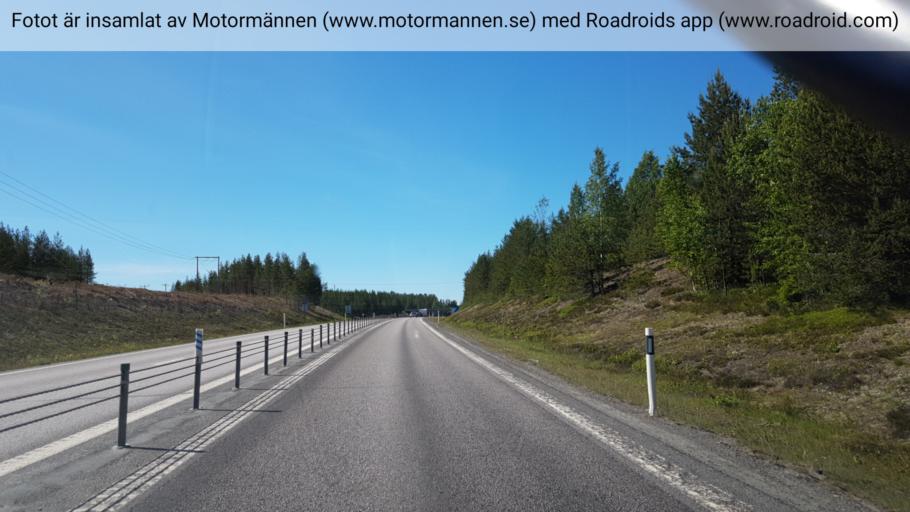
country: SE
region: Norrbotten
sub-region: Lulea Kommun
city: Gammelstad
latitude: 65.6019
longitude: 22.0489
